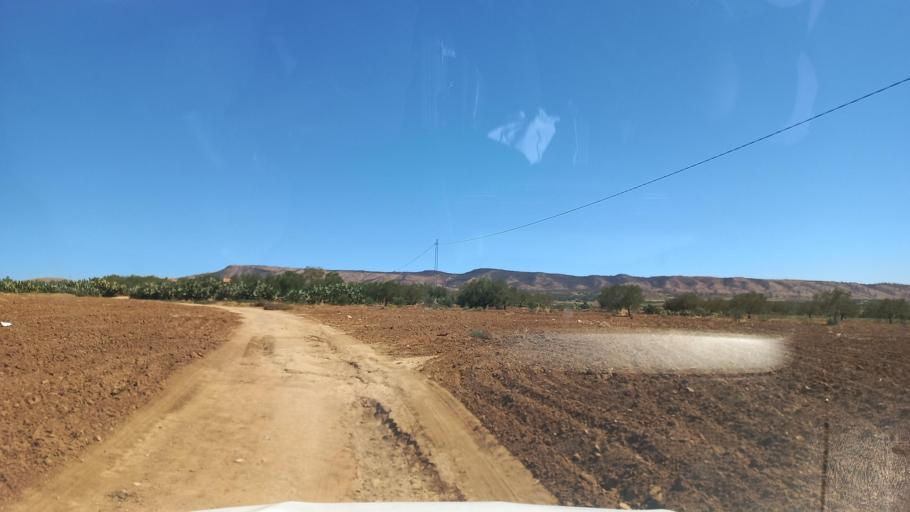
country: TN
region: Al Qasrayn
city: Sbiba
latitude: 35.3504
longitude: 9.1057
